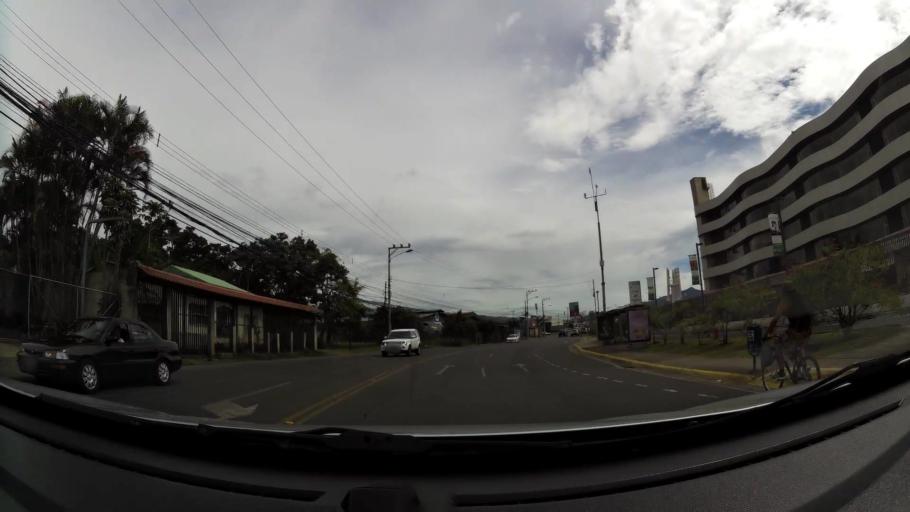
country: CR
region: San Jose
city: San Pedro
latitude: 9.9253
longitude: -84.0582
